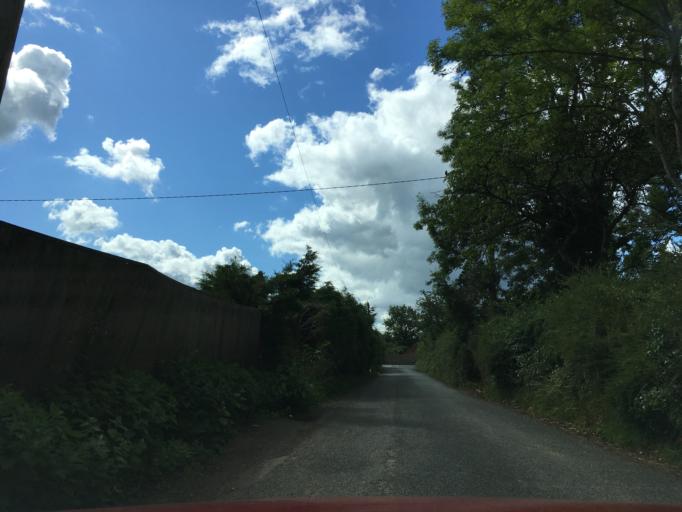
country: GB
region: England
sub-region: Gloucestershire
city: Newent
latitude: 51.8487
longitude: -2.3483
